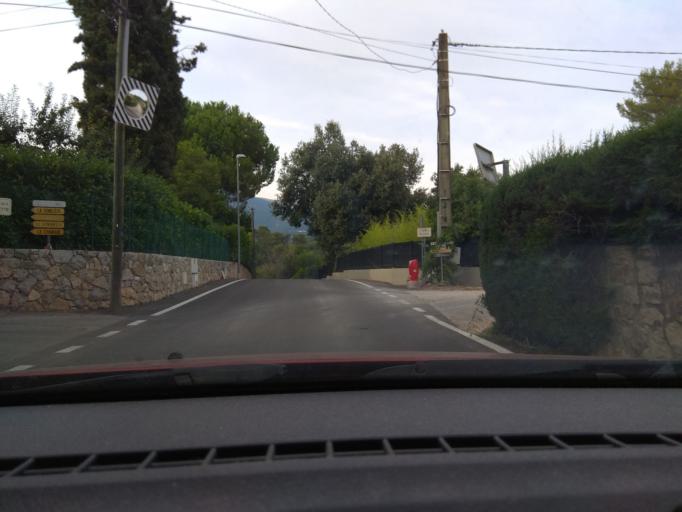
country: FR
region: Provence-Alpes-Cote d'Azur
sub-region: Departement des Alpes-Maritimes
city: Le Rouret
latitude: 43.6761
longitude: 7.0458
